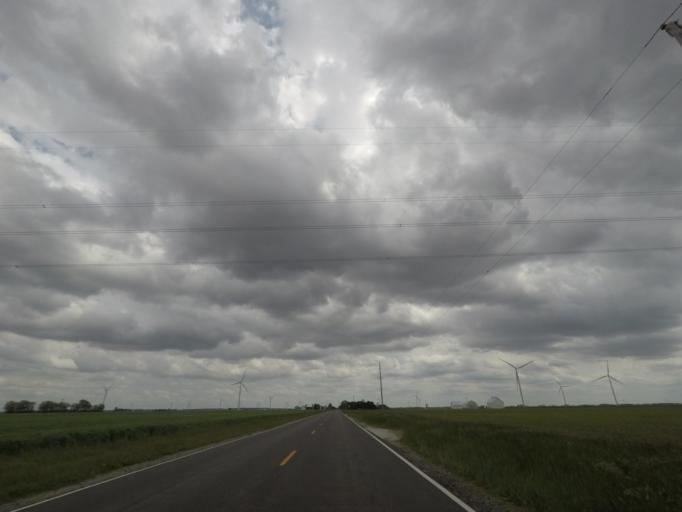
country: US
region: Illinois
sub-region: Macon County
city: Warrensburg
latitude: 40.0096
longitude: -89.0856
